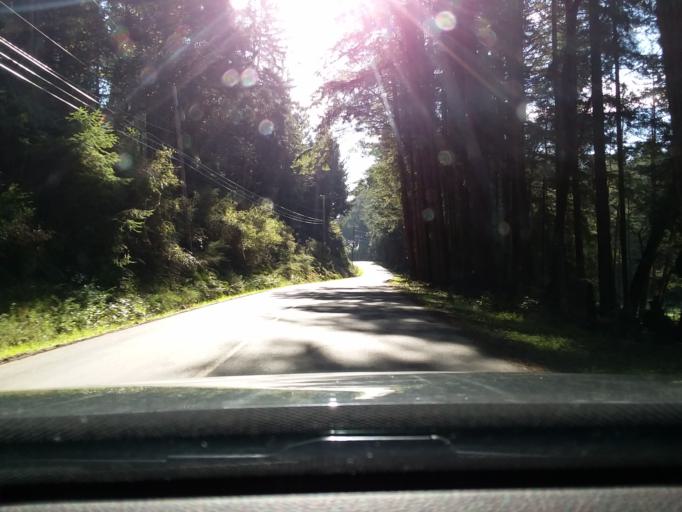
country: CA
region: British Columbia
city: North Cowichan
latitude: 48.9470
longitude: -123.5128
